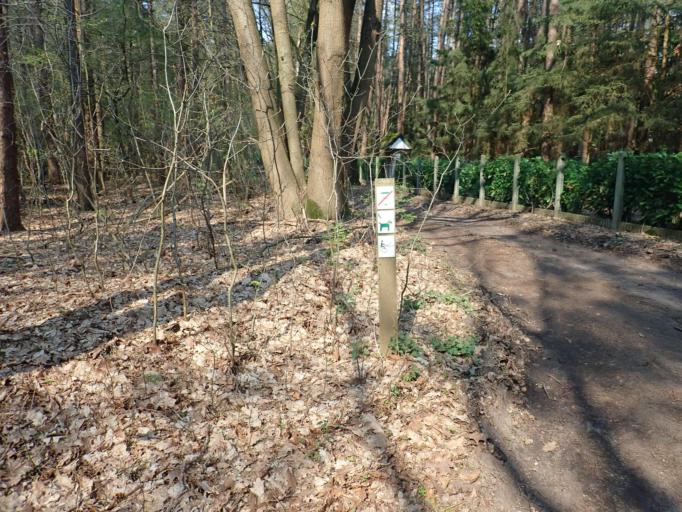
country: BE
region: Flanders
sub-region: Provincie Antwerpen
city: Essen
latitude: 51.4675
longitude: 4.5357
